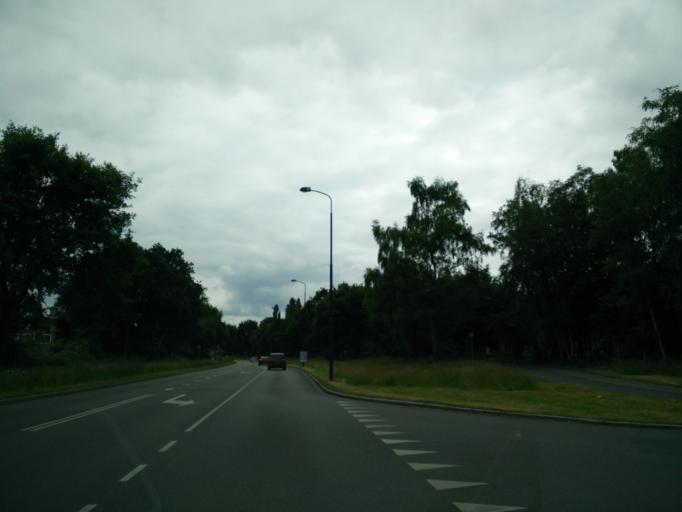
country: NL
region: Gelderland
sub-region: Gemeente Apeldoorn
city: Apeldoorn
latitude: 52.2041
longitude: 5.9294
